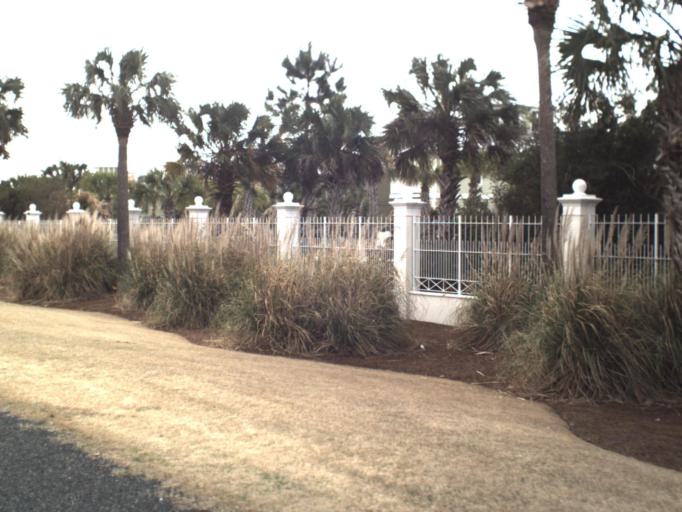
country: US
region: Florida
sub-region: Bay County
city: Laguna Beach
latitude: 30.2634
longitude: -85.9751
